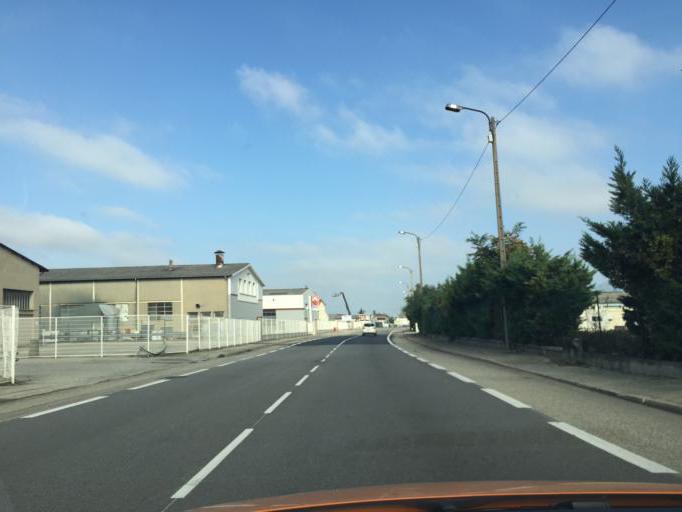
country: FR
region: Rhone-Alpes
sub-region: Departement de la Drome
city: Portes-les-Valence
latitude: 44.8965
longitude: 4.8836
